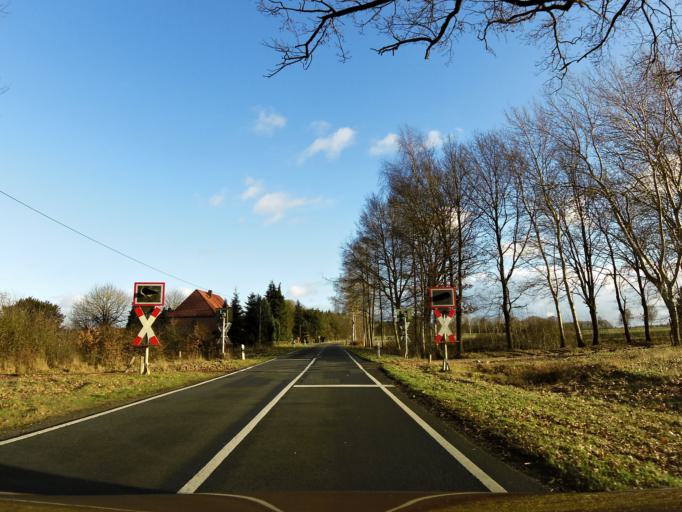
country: DE
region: Lower Saxony
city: Hauslingen
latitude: 52.8707
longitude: 9.3765
